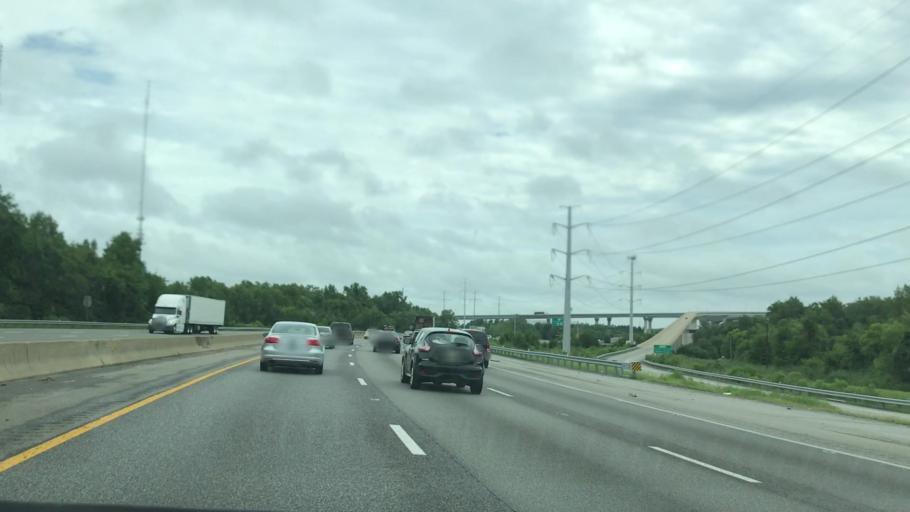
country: US
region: Virginia
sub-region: Chesterfield County
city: Bellwood
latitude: 37.4340
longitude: -77.4317
